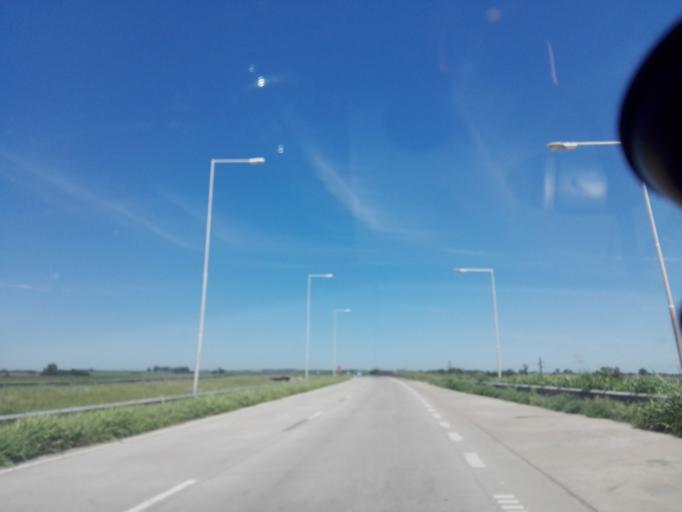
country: AR
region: Santa Fe
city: Canada de Gomez
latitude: -32.8542
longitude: -61.3459
